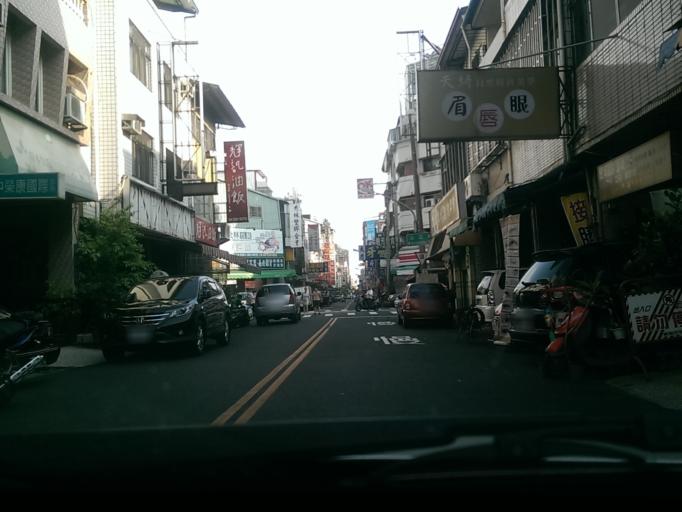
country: TW
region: Taiwan
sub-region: Taichung City
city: Taichung
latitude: 24.1495
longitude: 120.6589
